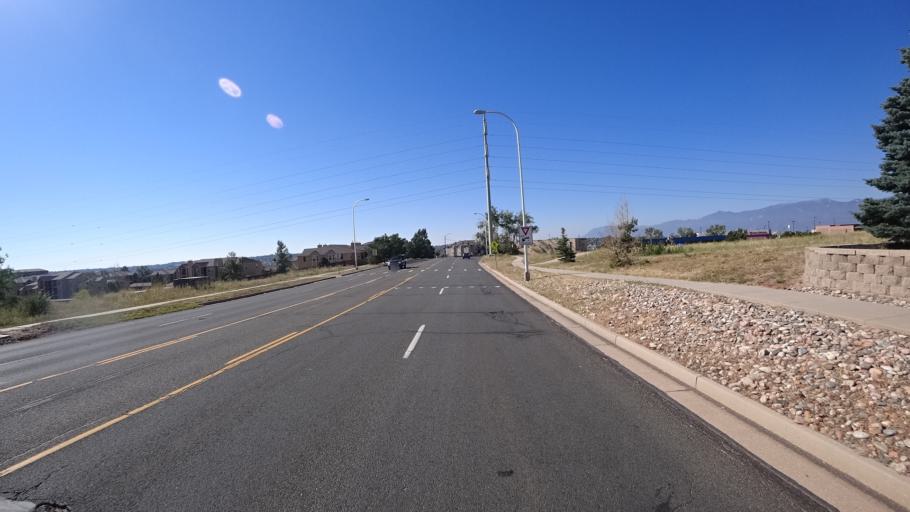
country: US
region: Colorado
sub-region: El Paso County
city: Black Forest
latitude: 38.9412
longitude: -104.7559
